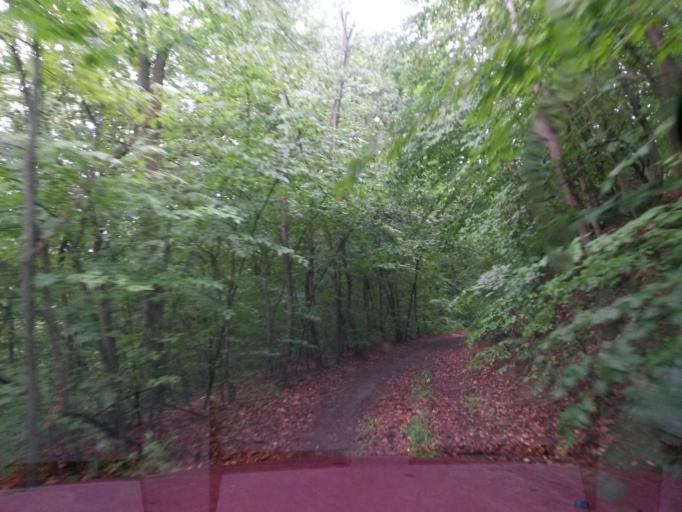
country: SK
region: Kosicky
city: Kosice
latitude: 48.7232
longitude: 21.1538
